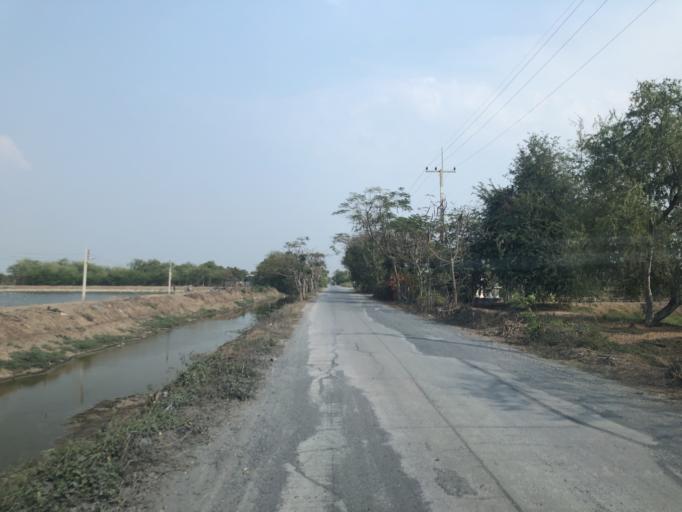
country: TH
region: Chachoengsao
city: Bang Pakong
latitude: 13.5114
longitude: 100.9274
